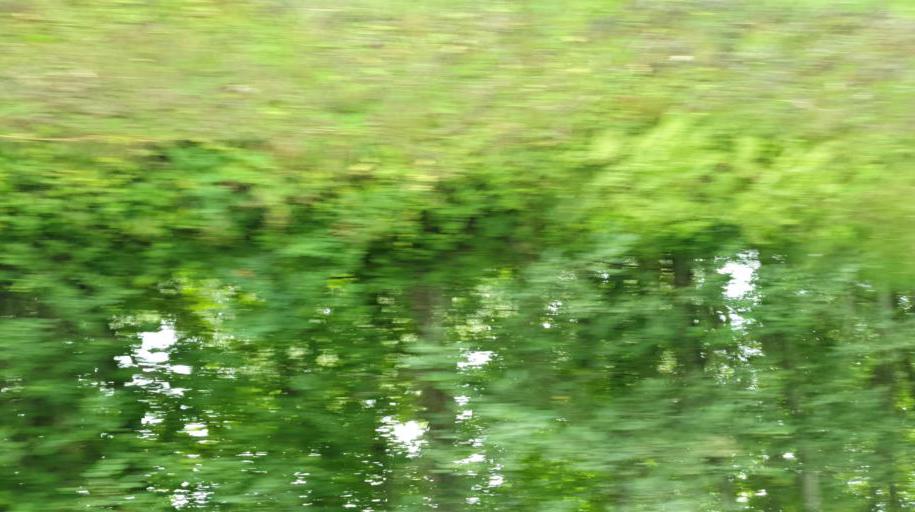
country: NO
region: Nord-Trondelag
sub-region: Stjordal
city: Stjordalshalsen
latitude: 63.4557
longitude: 10.9526
